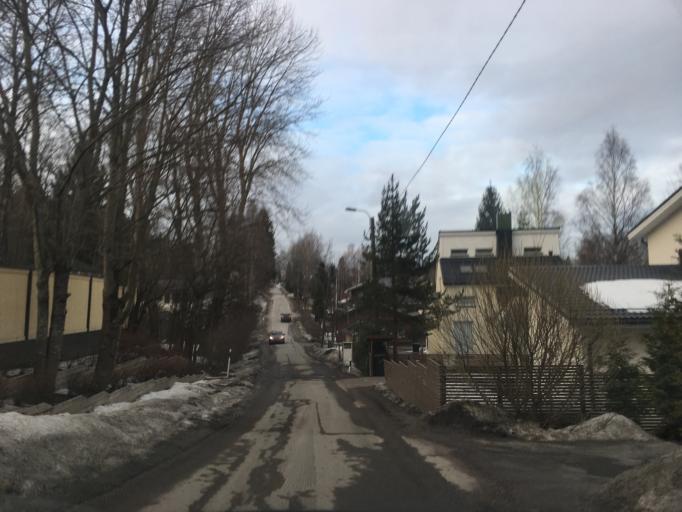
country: FI
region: Uusimaa
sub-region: Helsinki
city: Vantaa
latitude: 60.2652
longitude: 25.0893
